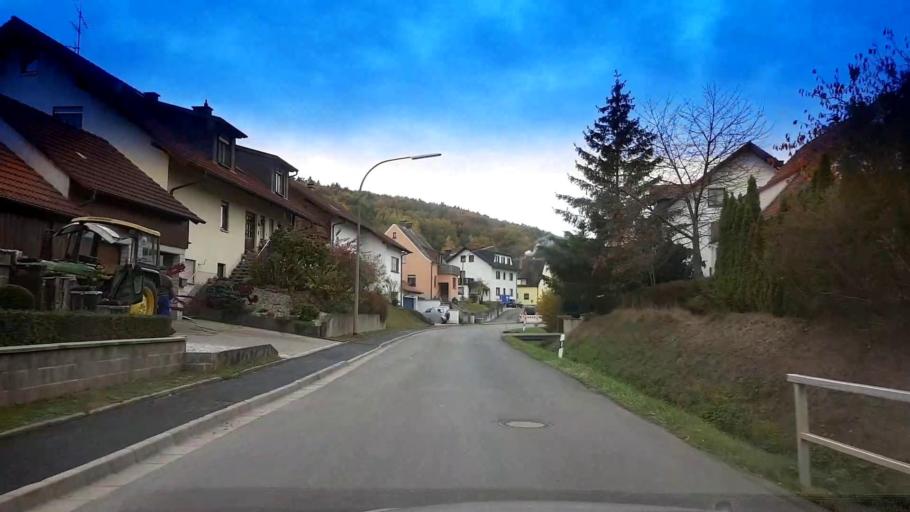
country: DE
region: Bavaria
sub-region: Upper Franconia
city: Viereth-Trunstadt
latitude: 49.9199
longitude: 10.7751
